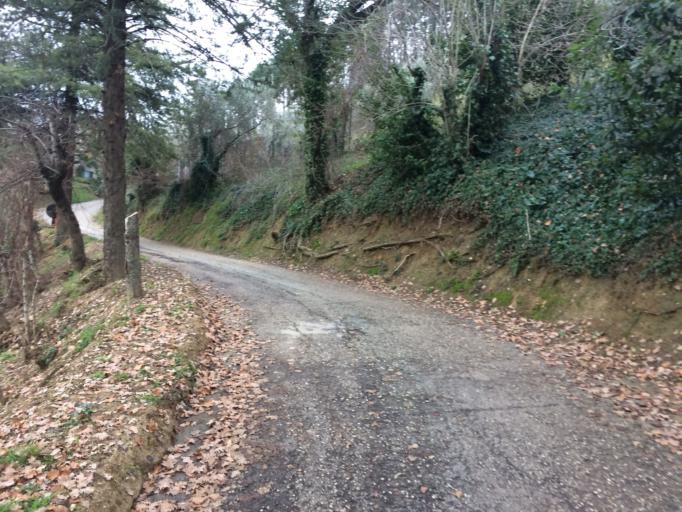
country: IT
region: Umbria
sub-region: Provincia di Perugia
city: Perugia
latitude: 43.1046
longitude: 12.3986
